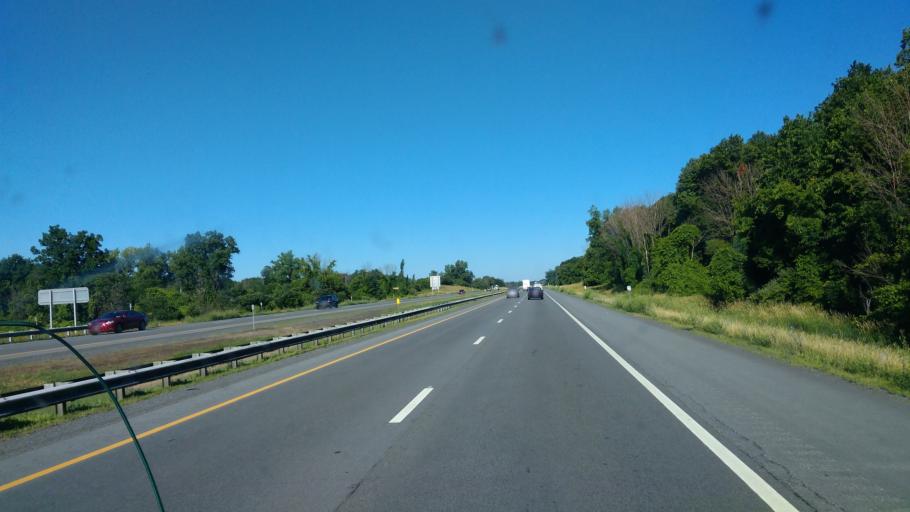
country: US
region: New York
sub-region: Monroe County
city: Scottsville
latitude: 43.0452
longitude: -77.7554
